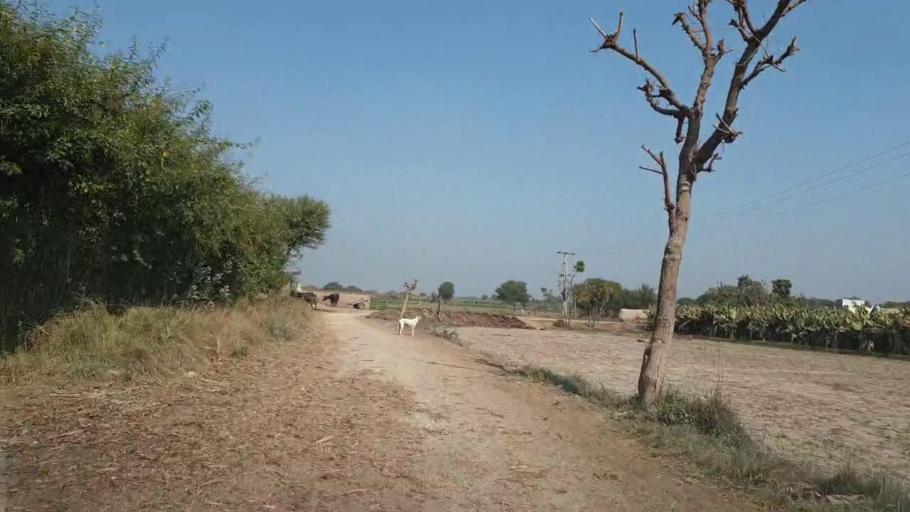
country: PK
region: Sindh
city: Tando Jam
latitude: 25.4965
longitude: 68.4760
